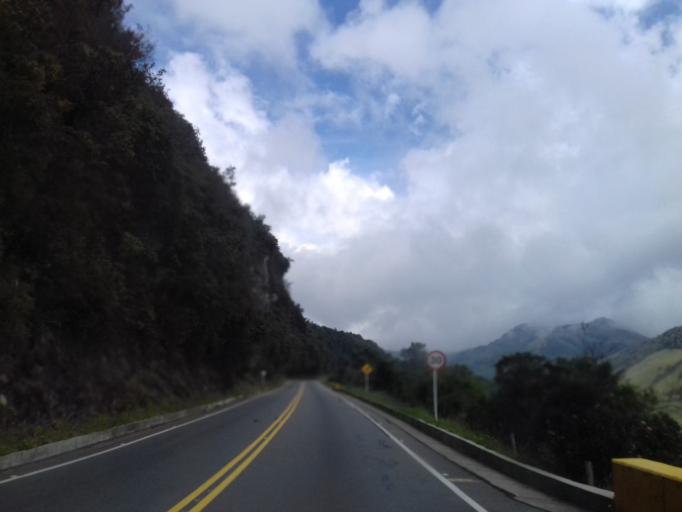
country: CO
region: Caldas
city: Villamaria
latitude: 5.0141
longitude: -75.3483
